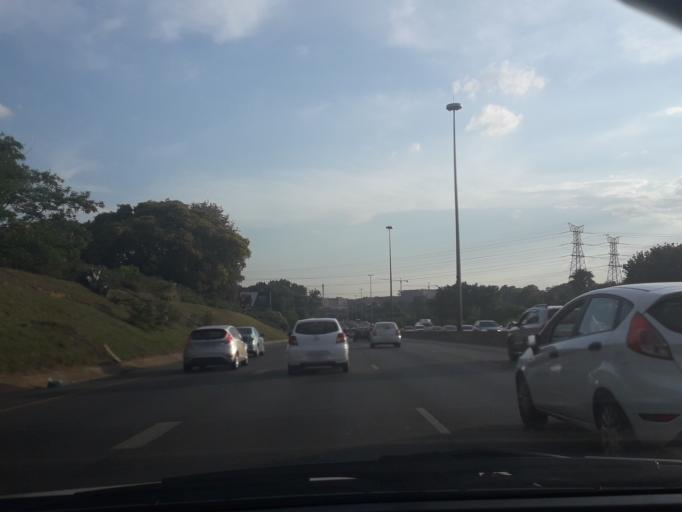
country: ZA
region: Gauteng
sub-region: City of Johannesburg Metropolitan Municipality
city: Johannesburg
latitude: -26.1180
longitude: 28.0740
